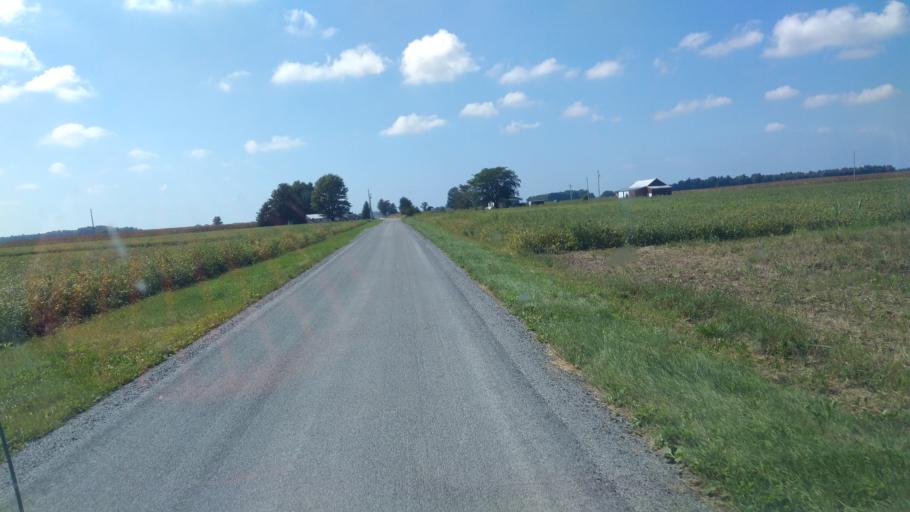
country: US
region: Ohio
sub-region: Hardin County
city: Ada
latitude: 40.7619
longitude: -83.7452
